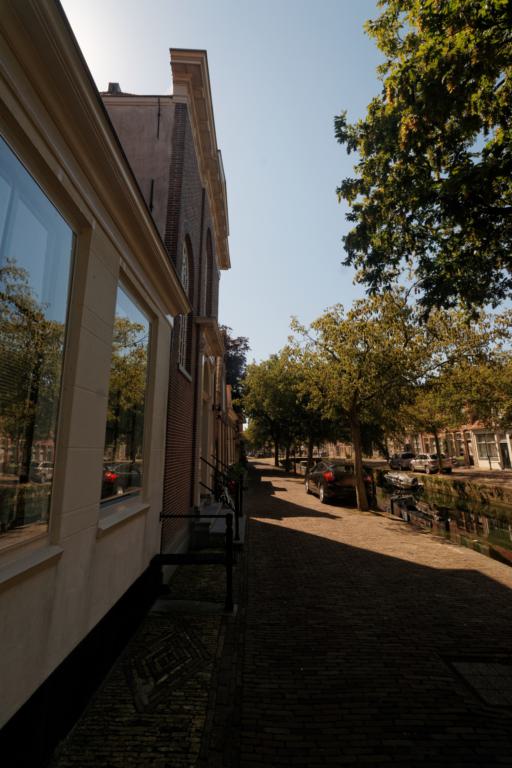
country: NL
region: North Holland
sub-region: Gemeente Enkhuizen
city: Enkhuizen
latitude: 52.7033
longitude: 5.2939
